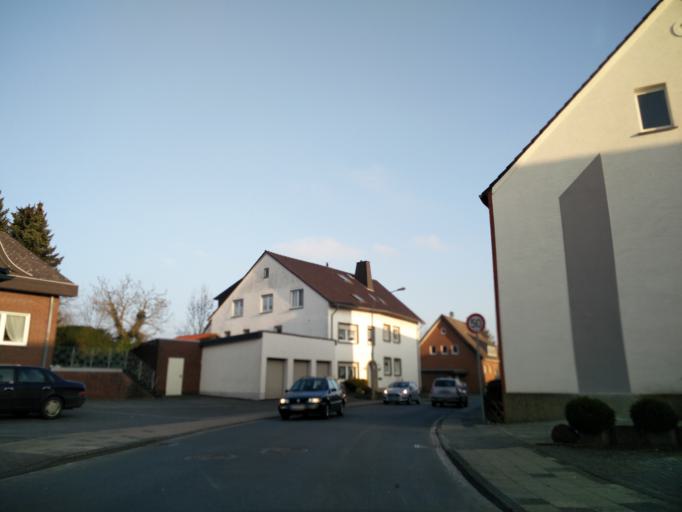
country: DE
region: North Rhine-Westphalia
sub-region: Regierungsbezirk Detmold
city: Paderborn
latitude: 51.6913
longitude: 8.6924
